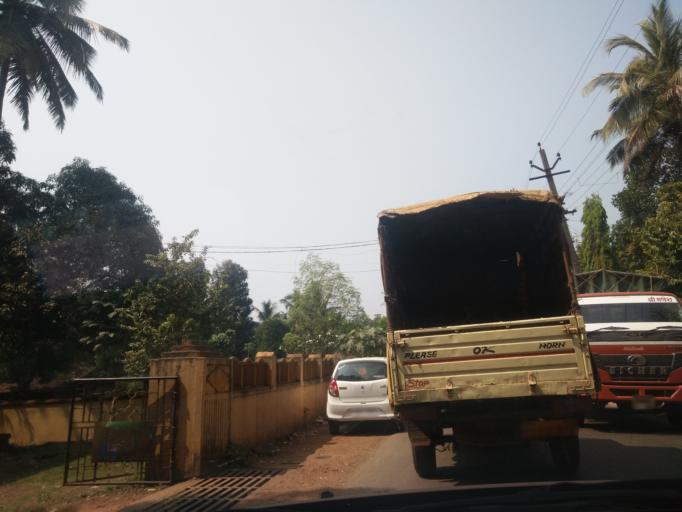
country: IN
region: Goa
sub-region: North Goa
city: Aldona
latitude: 15.6194
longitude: 73.9007
